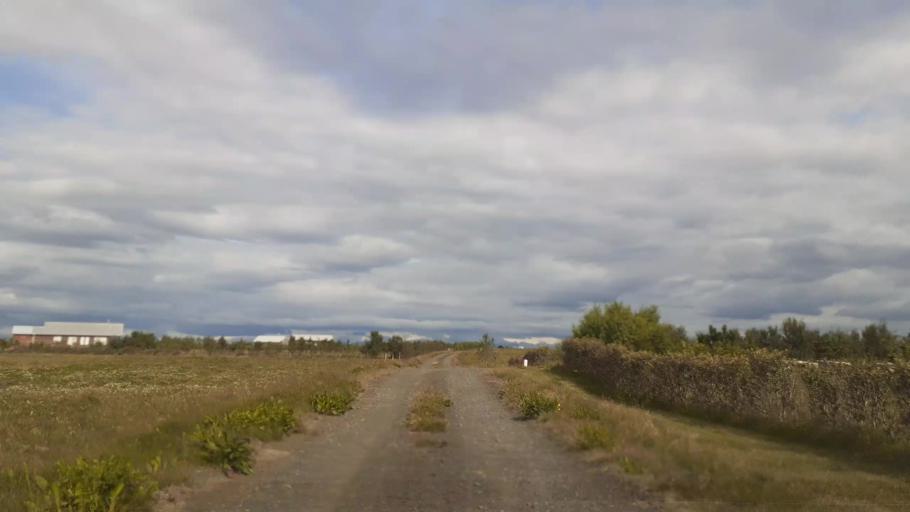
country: IS
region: South
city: Vestmannaeyjar
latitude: 63.7715
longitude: -20.2979
